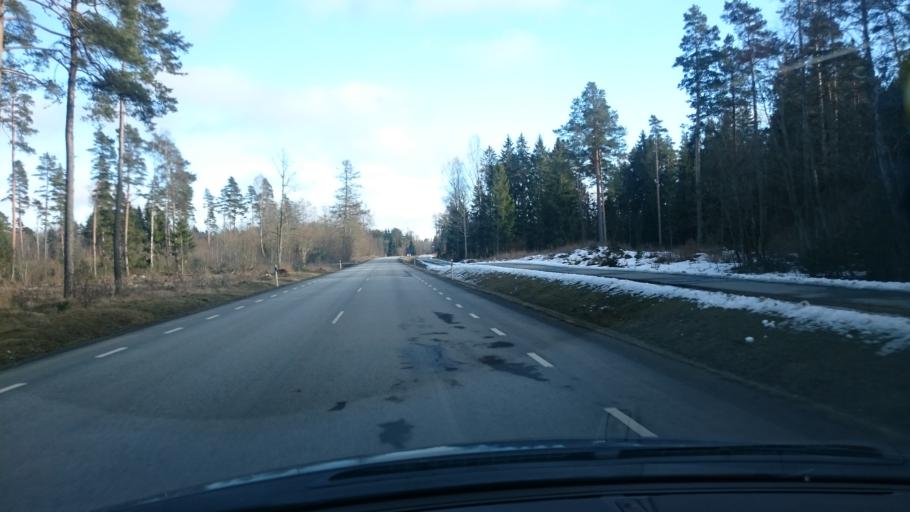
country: EE
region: Harju
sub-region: Kiili vald
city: Kiili
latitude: 59.3519
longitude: 24.7891
